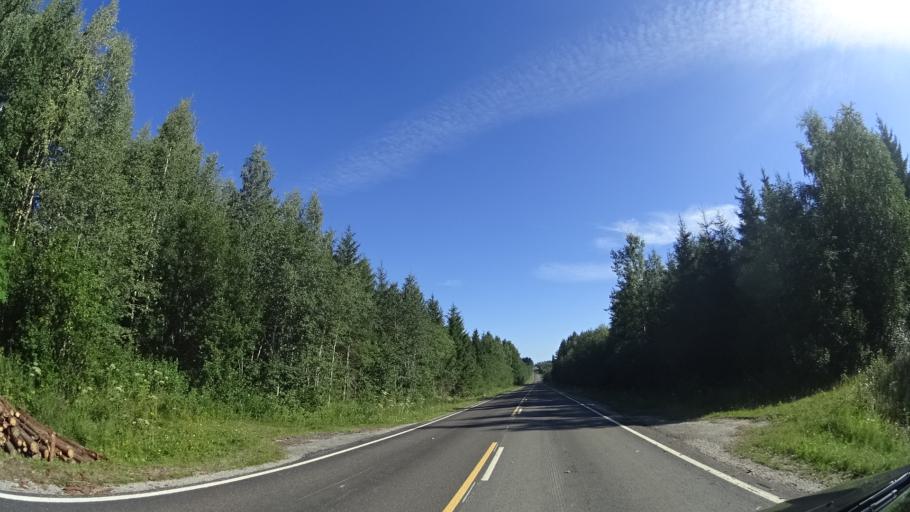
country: FI
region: Central Finland
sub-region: Jyvaeskylae
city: Petaejaevesi
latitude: 62.3653
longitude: 25.3194
